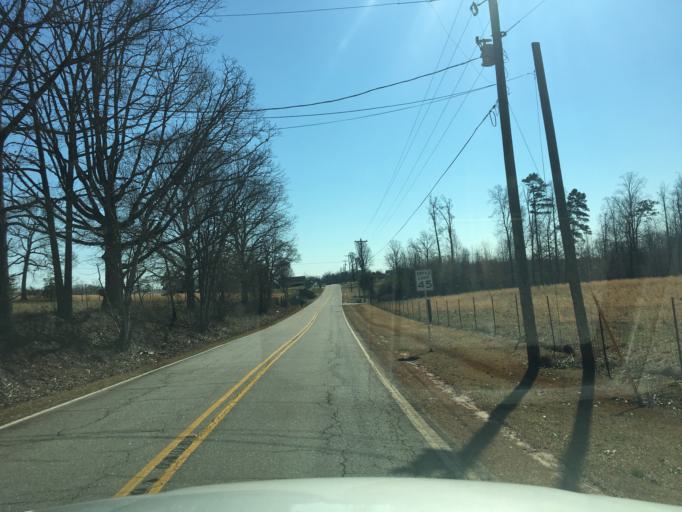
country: US
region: South Carolina
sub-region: Pickens County
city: Liberty
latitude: 34.8175
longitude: -82.7710
